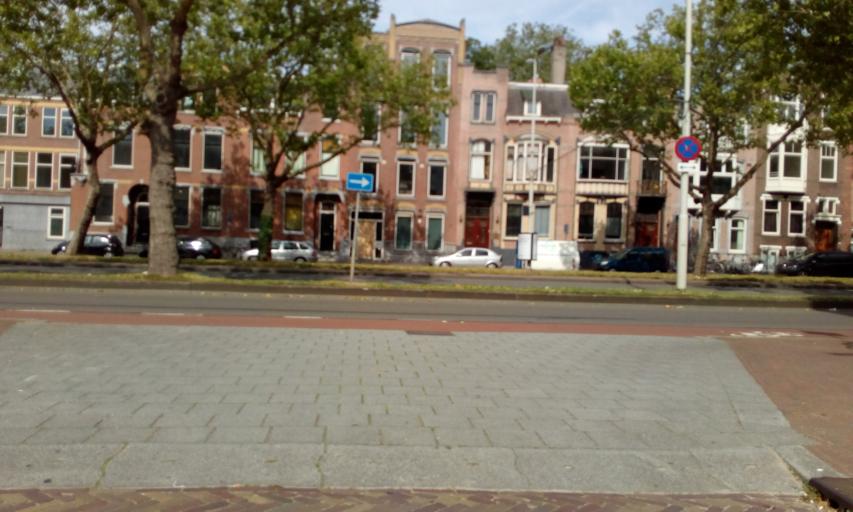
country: NL
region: South Holland
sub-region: Gemeente Rotterdam
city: Delfshaven
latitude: 51.9174
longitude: 4.4633
